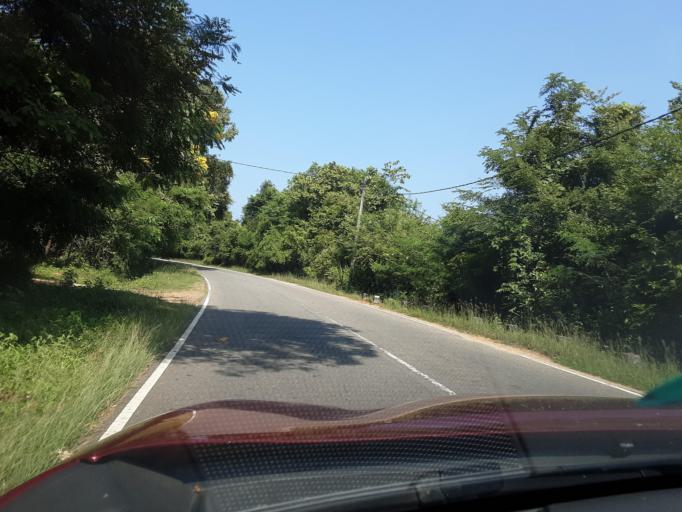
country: LK
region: Uva
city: Badulla
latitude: 7.2716
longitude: 81.0522
